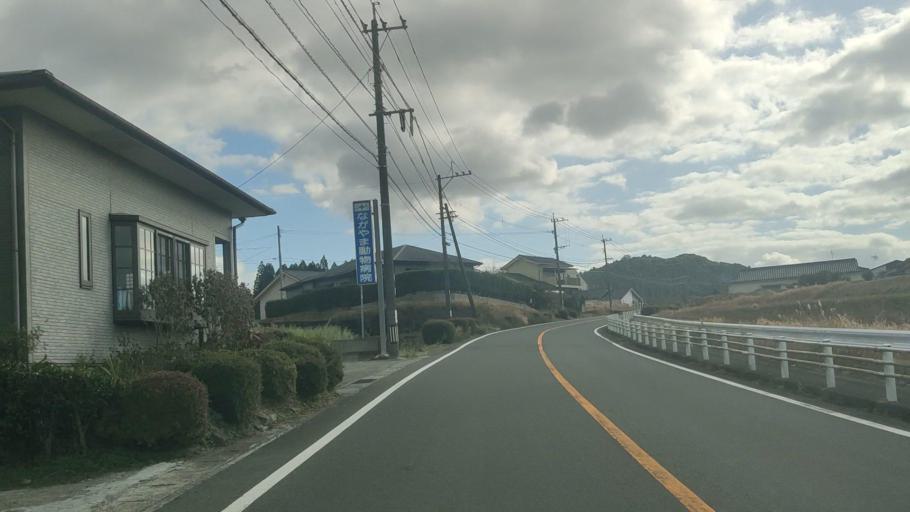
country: JP
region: Kagoshima
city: Kajiki
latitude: 31.8350
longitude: 130.6871
